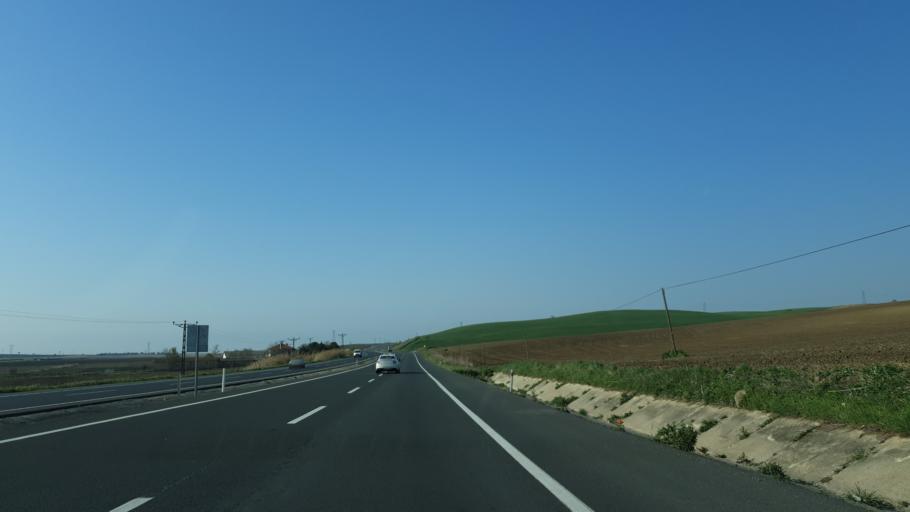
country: TR
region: Tekirdag
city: Corlu
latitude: 41.0441
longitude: 27.7326
